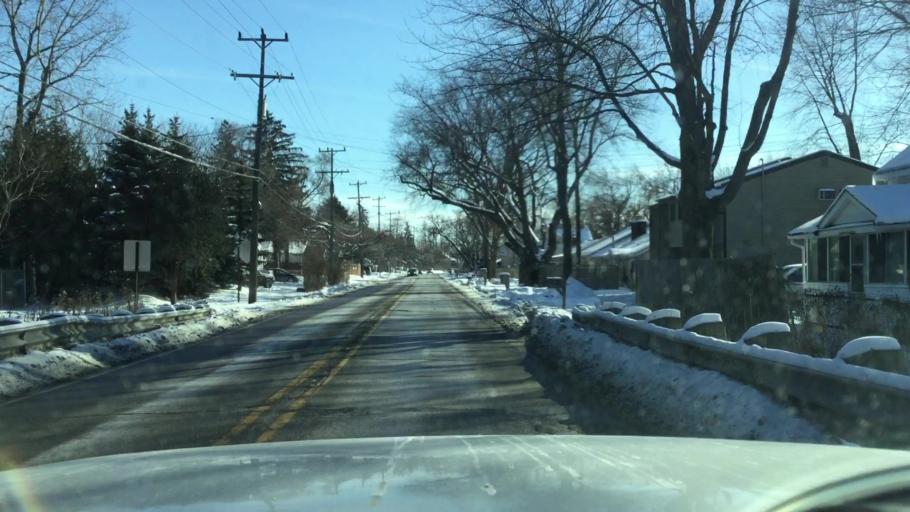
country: US
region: Michigan
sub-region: Oakland County
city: Keego Harbor
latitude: 42.6216
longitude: -83.3537
